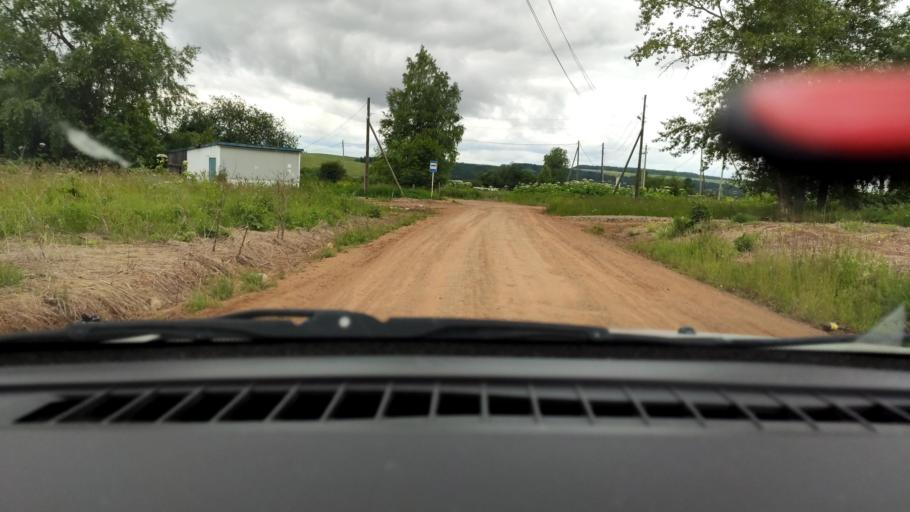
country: RU
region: Perm
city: Chaykovskaya
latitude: 58.1443
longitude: 55.5727
